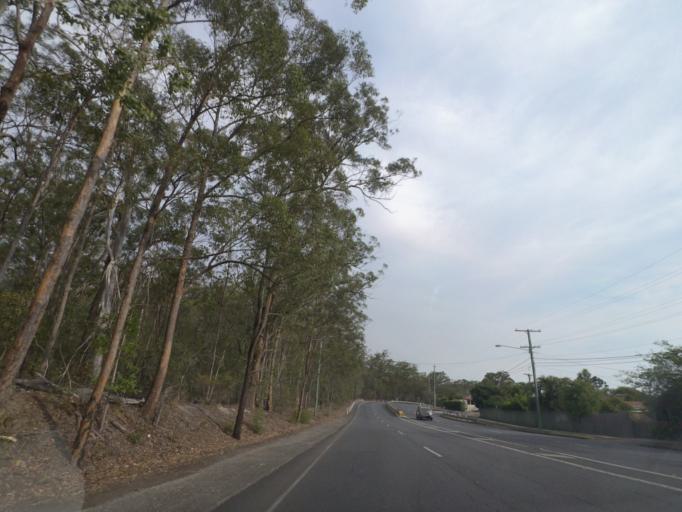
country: AU
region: Queensland
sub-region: Brisbane
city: Coopers Plains
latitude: -27.5497
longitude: 153.0411
